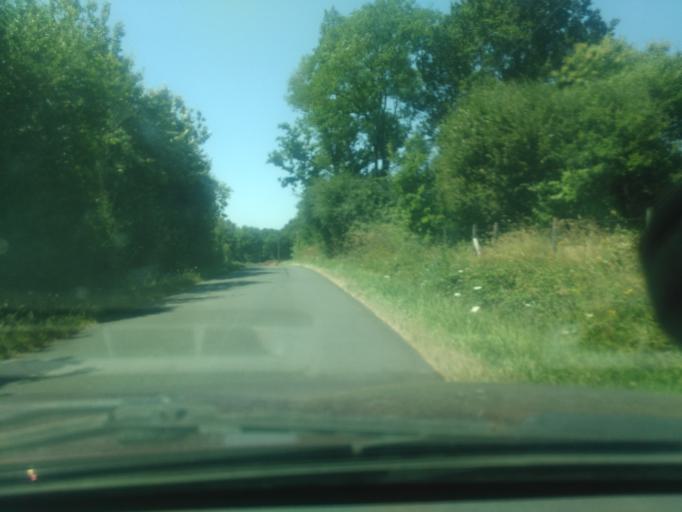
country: FR
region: Pays de la Loire
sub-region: Departement de la Vendee
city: Dompierre-sur-Yon
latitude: 46.7192
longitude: -1.3605
